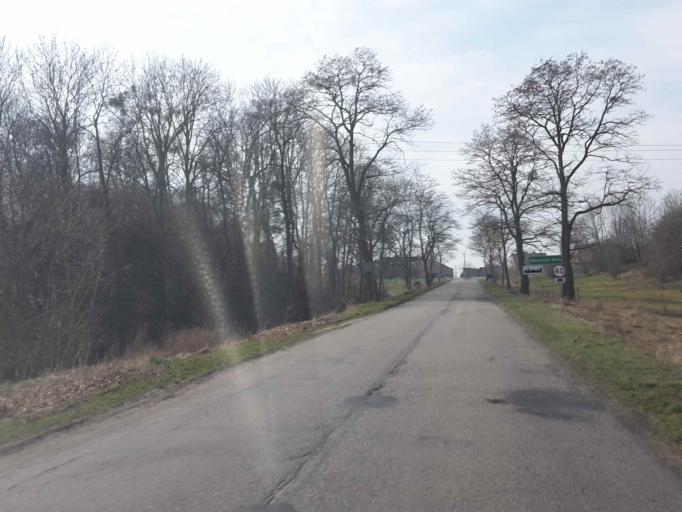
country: PL
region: Kujawsko-Pomorskie
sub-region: Powiat nakielski
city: Szubin
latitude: 53.0726
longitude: 17.7190
